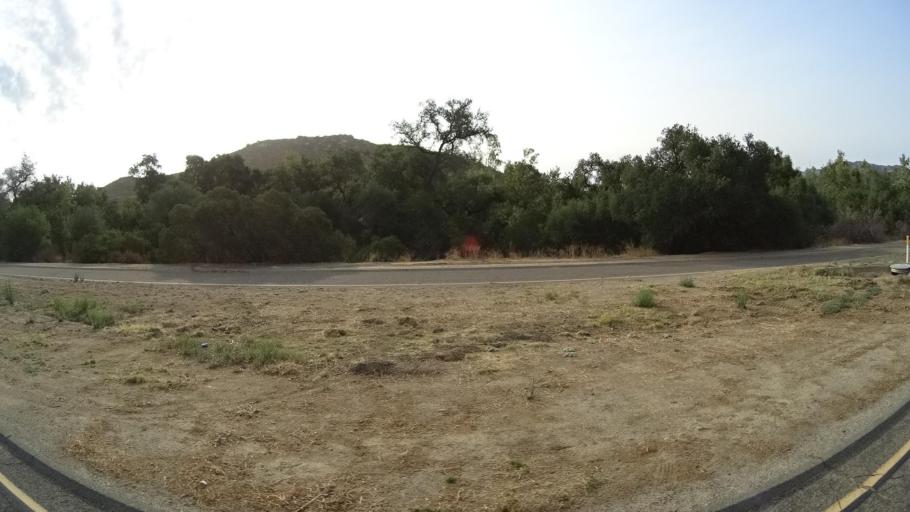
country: US
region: California
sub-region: San Diego County
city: San Diego Country Estates
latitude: 33.0232
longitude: -116.8008
